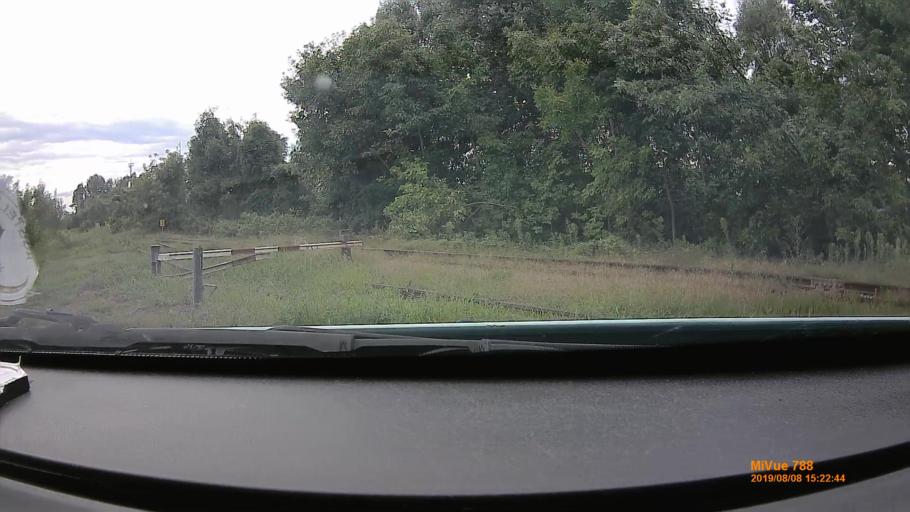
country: HU
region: Szabolcs-Szatmar-Bereg
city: Tunyogmatolcs
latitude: 47.9591
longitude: 22.4412
